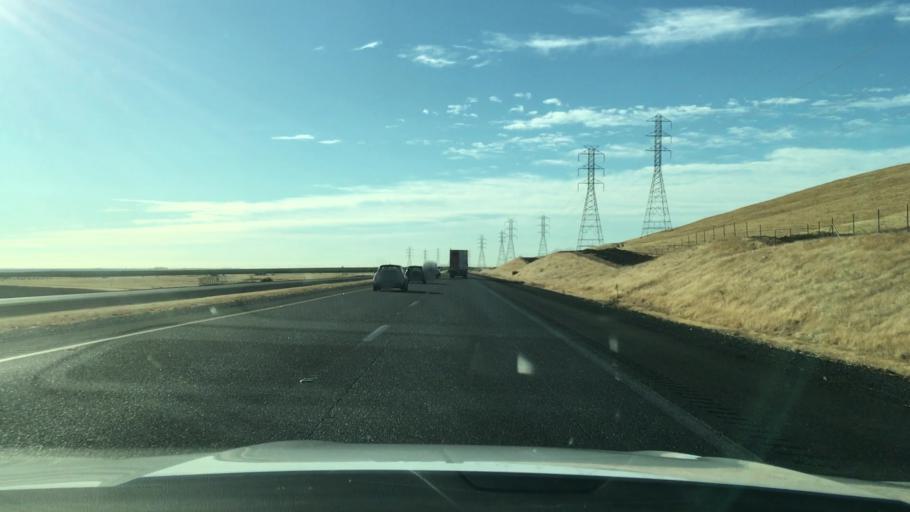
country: US
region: California
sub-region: Merced County
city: Los Banos
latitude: 36.8981
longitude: -120.8089
